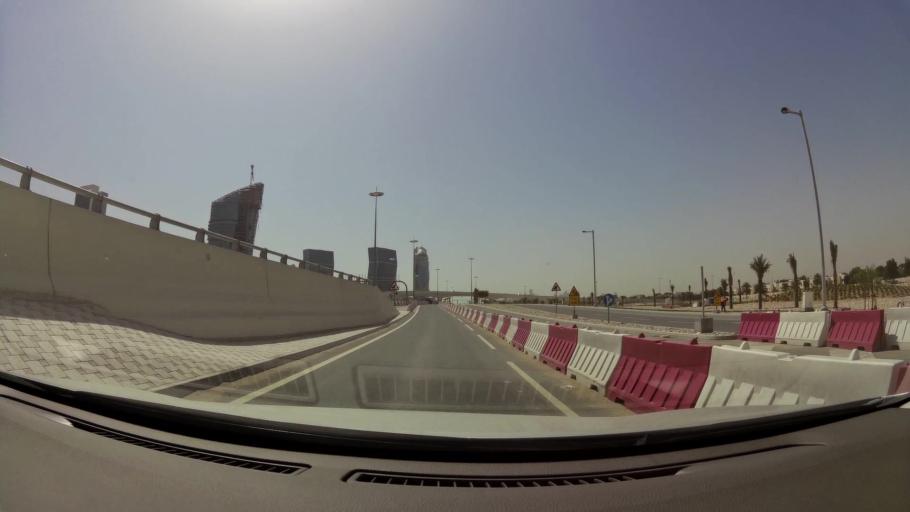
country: QA
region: Baladiyat ad Dawhah
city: Doha
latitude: 25.3858
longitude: 51.5193
